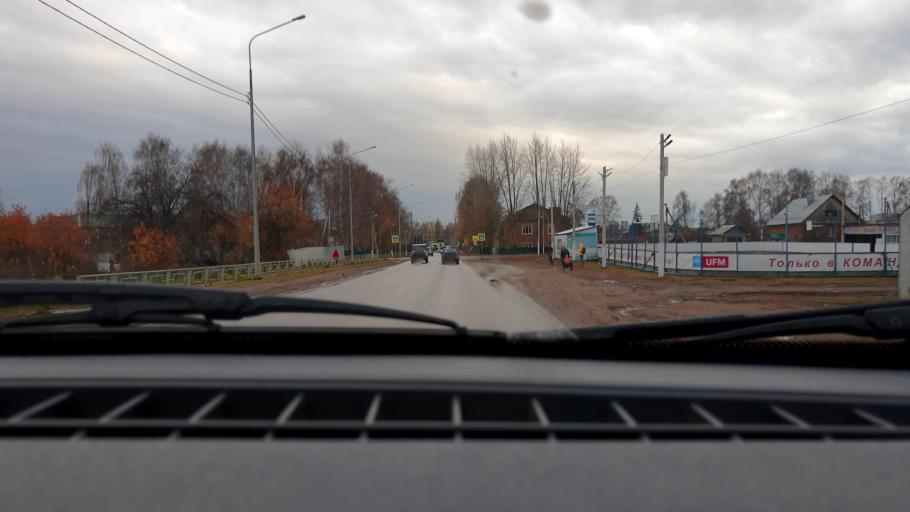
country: RU
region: Bashkortostan
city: Mikhaylovka
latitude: 54.8068
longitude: 55.8898
